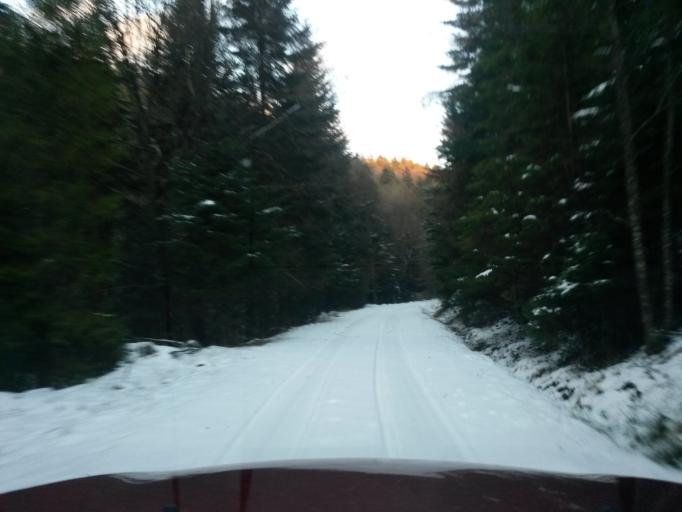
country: SK
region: Kosicky
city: Medzev
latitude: 48.7841
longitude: 20.8184
